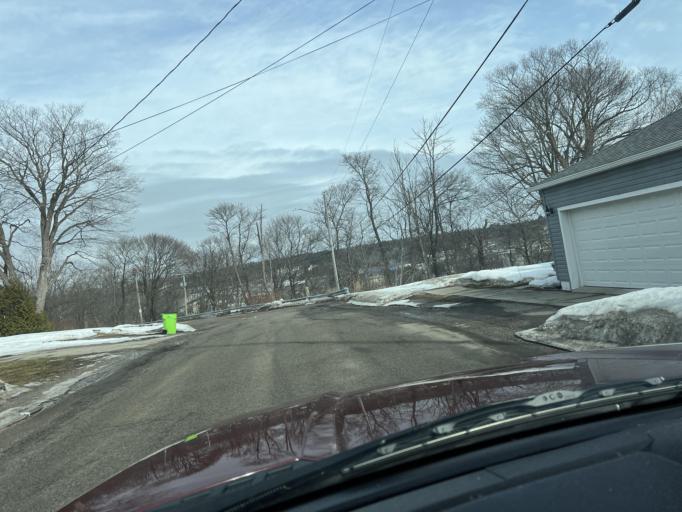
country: US
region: Michigan
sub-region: Mackinac County
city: Saint Ignace
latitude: 45.8686
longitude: -84.7325
